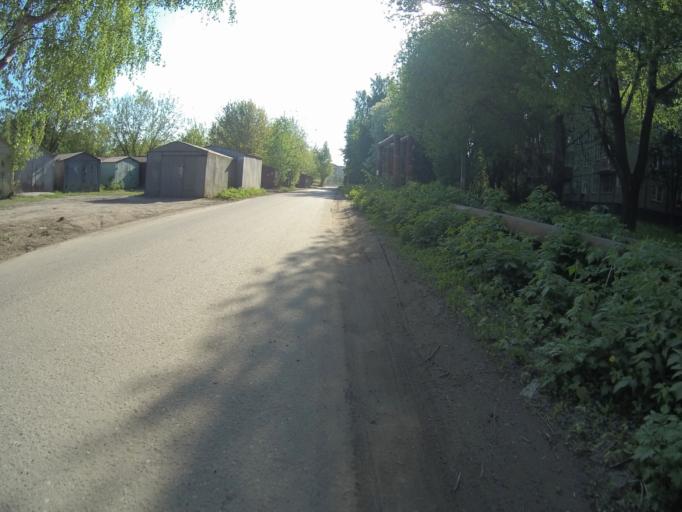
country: RU
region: Vladimir
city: Bogolyubovo
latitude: 56.1727
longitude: 40.4833
